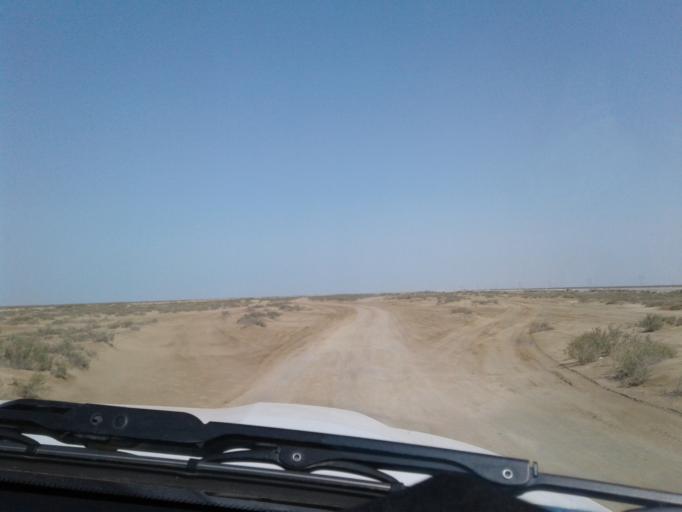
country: IR
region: Golestan
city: Gomishan
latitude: 37.8590
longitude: 53.8795
